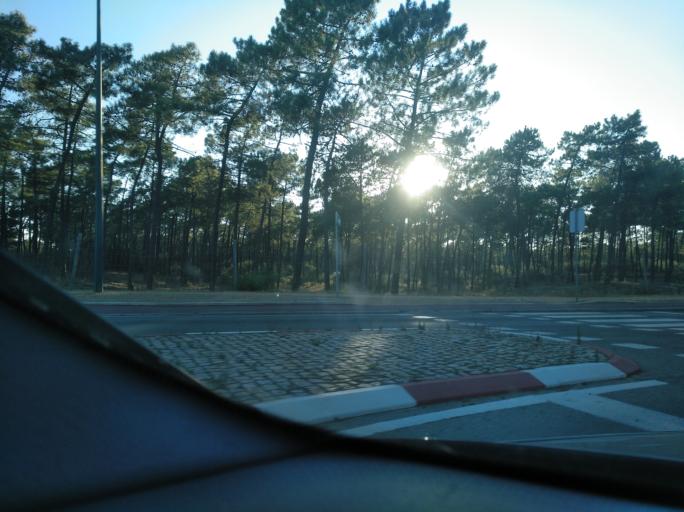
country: PT
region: Faro
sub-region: Vila Real de Santo Antonio
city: Vila Real de Santo Antonio
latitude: 37.1861
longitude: -7.4216
